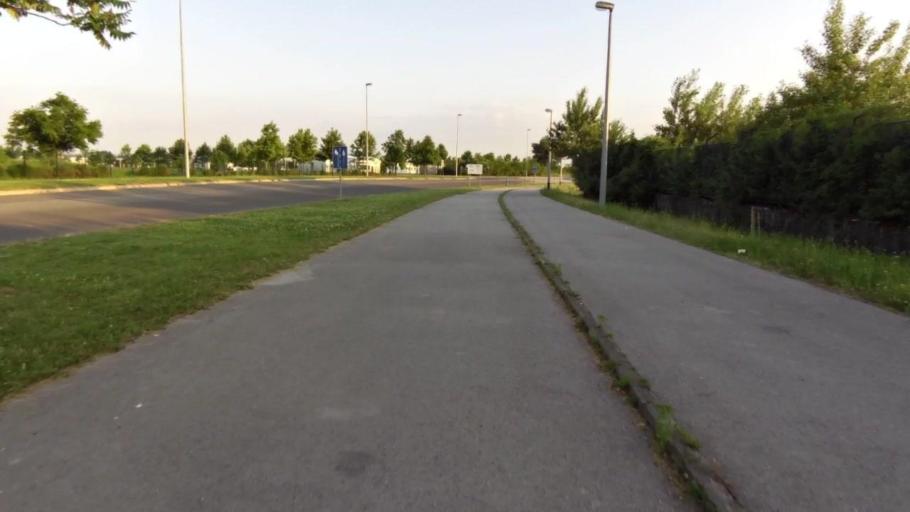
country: HR
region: Zagrebacka
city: Micevec
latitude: 45.7888
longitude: 16.0790
